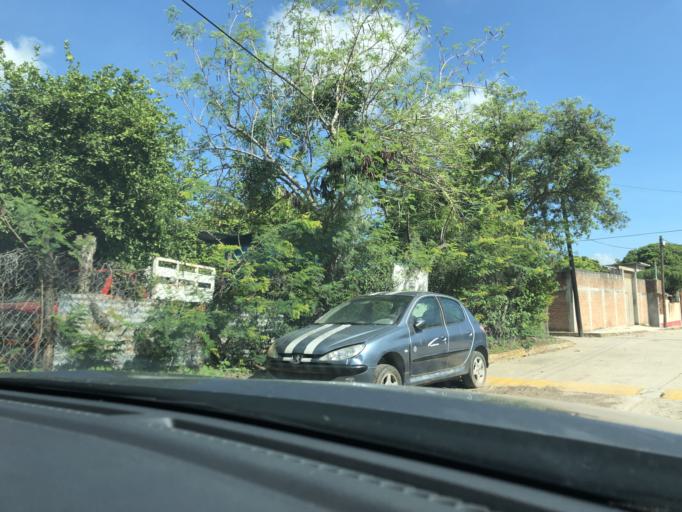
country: MX
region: Oaxaca
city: San Jeronimo Ixtepec
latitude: 16.5582
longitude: -95.1064
